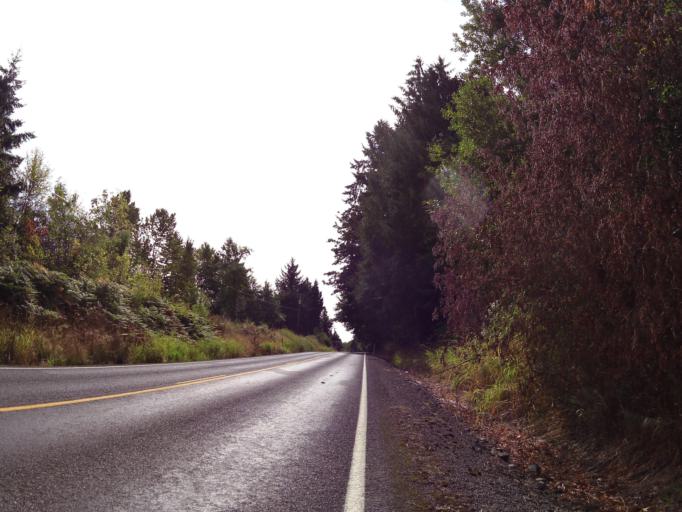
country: US
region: Washington
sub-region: Lewis County
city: Chehalis
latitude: 46.6335
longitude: -122.9704
